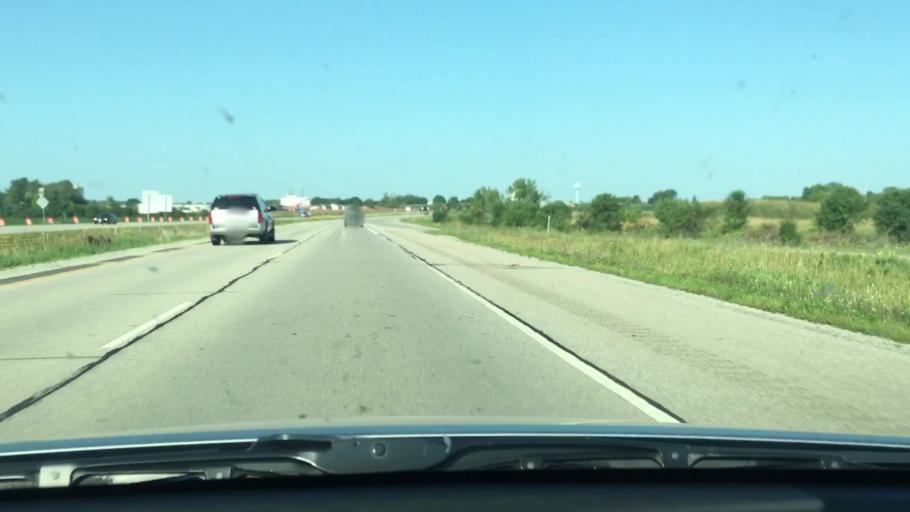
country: US
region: Wisconsin
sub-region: Outagamie County
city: Kaukauna
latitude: 44.2990
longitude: -88.2743
